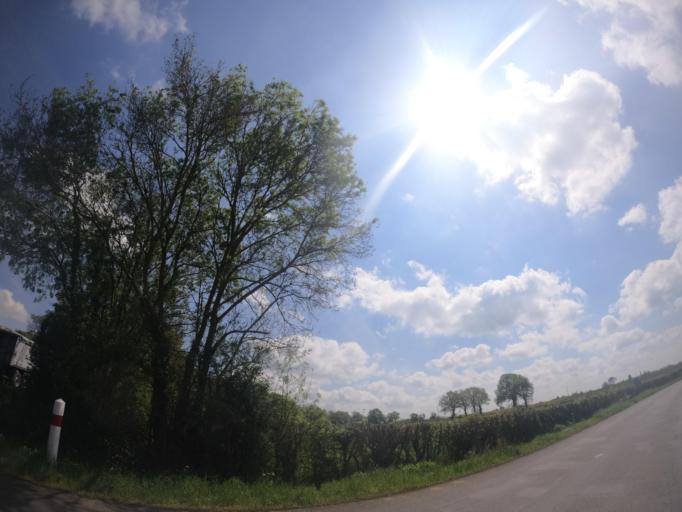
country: FR
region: Poitou-Charentes
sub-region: Departement des Deux-Sevres
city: Saint-Varent
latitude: 46.8685
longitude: -0.2437
